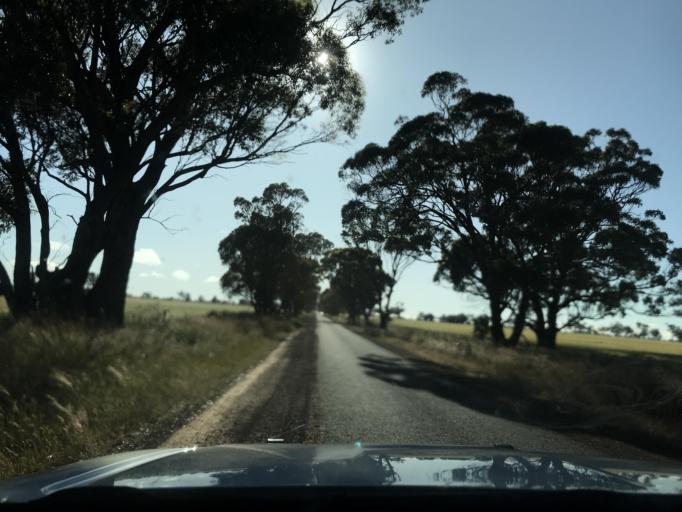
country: AU
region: Victoria
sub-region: Horsham
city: Horsham
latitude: -36.6916
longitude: 141.5401
